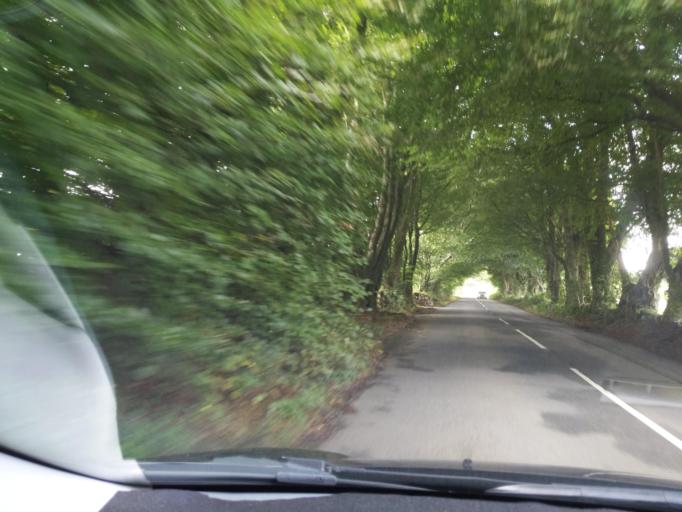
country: GB
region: England
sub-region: Cornwall
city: Callington
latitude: 50.5078
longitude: -4.3012
